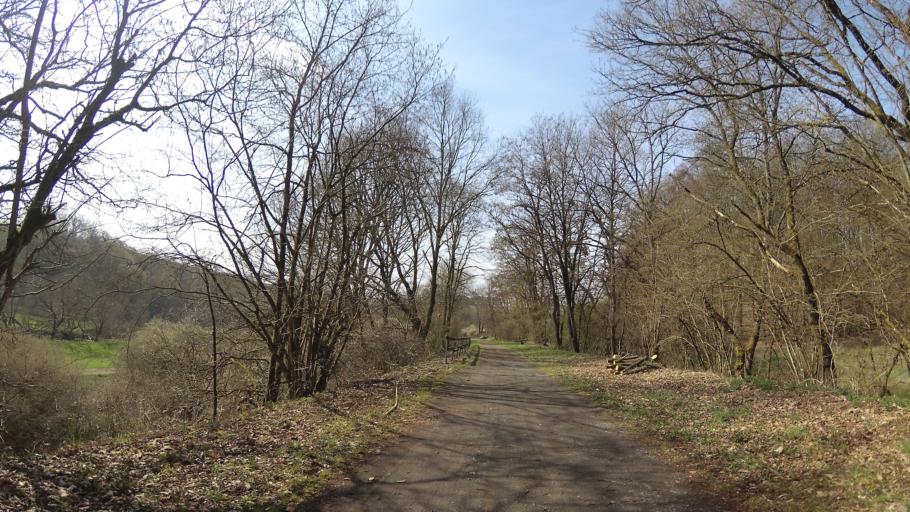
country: DE
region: Rheinland-Pfalz
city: Borsborn
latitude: 49.4260
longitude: 7.4263
